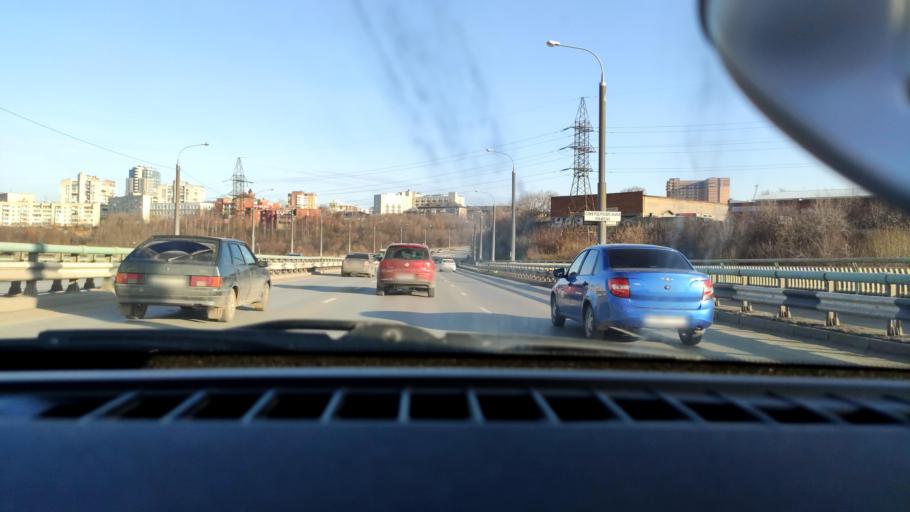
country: RU
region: Perm
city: Perm
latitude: 57.9848
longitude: 56.2315
